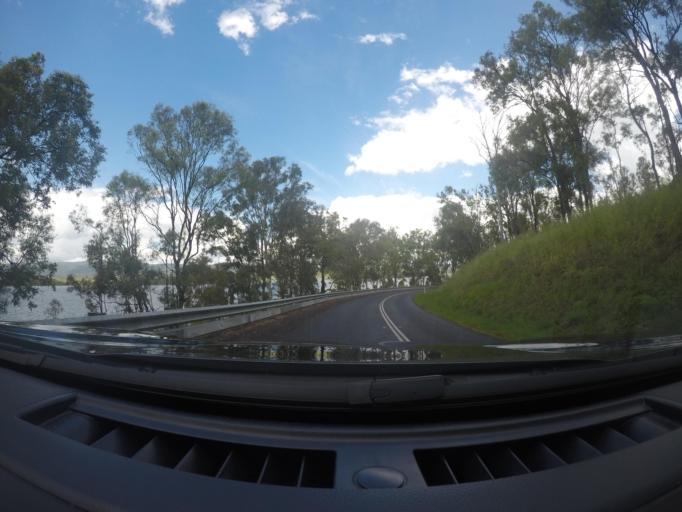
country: AU
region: Queensland
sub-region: Moreton Bay
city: Woodford
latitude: -27.0887
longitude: 152.5623
